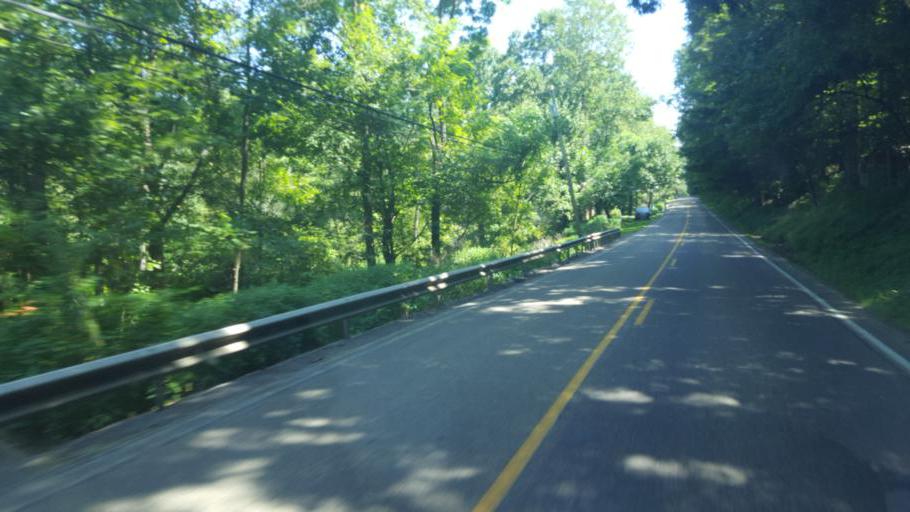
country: US
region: Pennsylvania
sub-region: Clarion County
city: Knox
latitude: 41.1684
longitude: -79.6897
